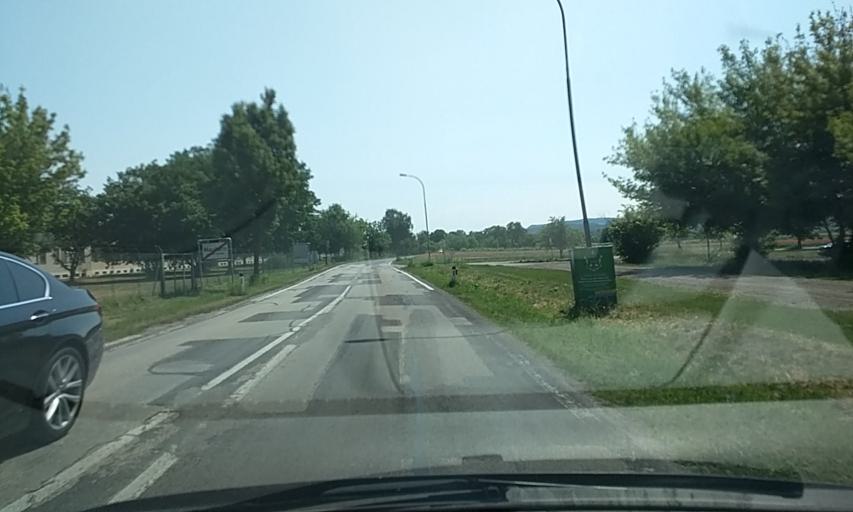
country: AT
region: Lower Austria
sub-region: Politischer Bezirk Krems
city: Weinzierl bei Krems
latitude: 48.3915
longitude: 15.5854
